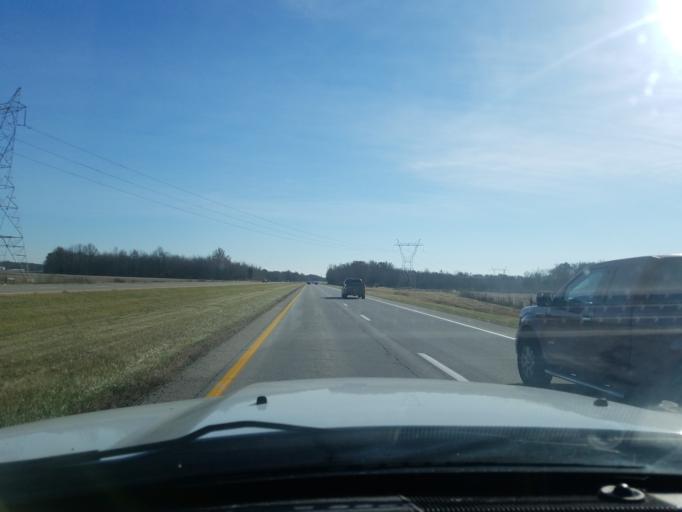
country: US
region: Ohio
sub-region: Brown County
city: Mount Orab
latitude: 39.0321
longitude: -83.8926
